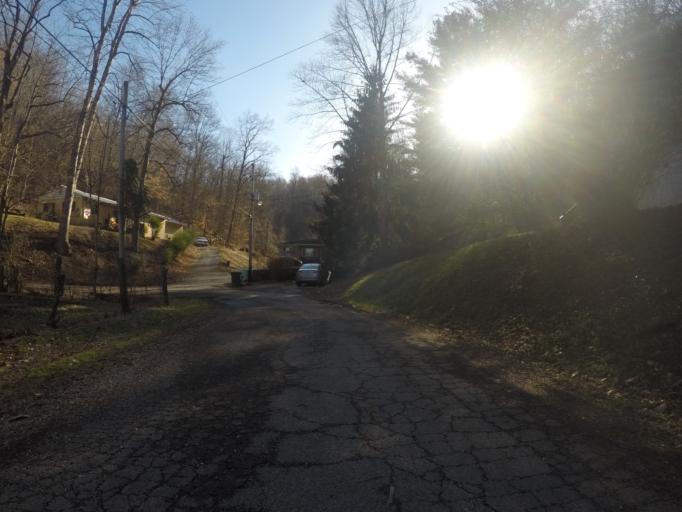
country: US
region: Ohio
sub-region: Lawrence County
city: Burlington
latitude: 38.3918
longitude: -82.4984
